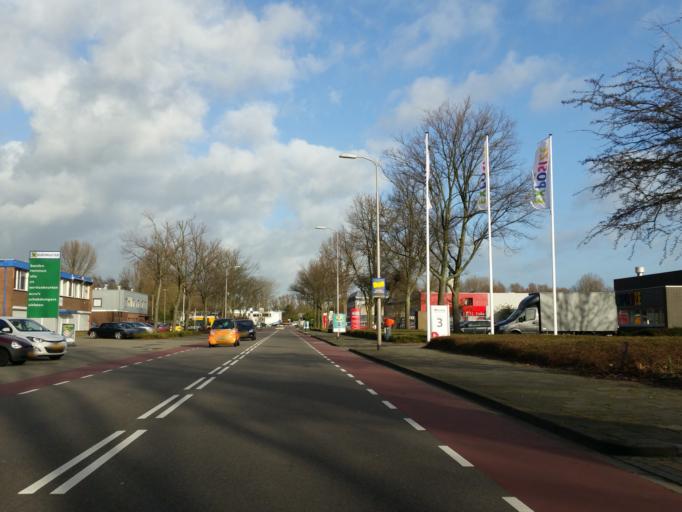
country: NL
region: South Holland
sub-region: Gemeente Zoetermeer
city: Zoetermeer
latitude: 52.0517
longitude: 4.5109
